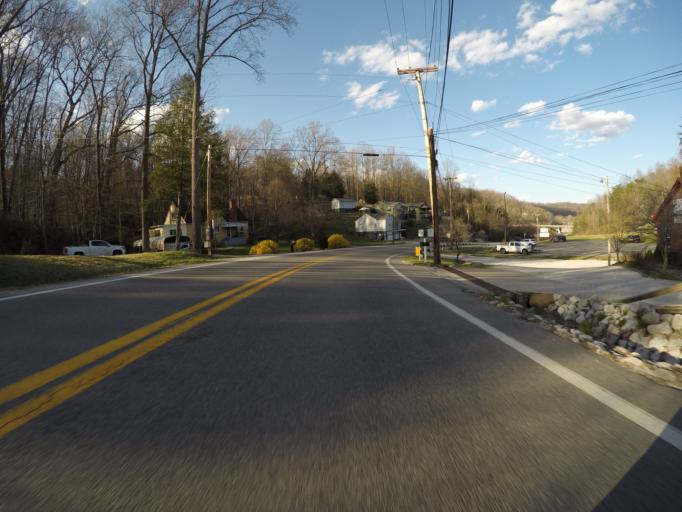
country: US
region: West Virginia
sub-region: Kanawha County
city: Charleston
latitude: 38.3907
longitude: -81.5926
